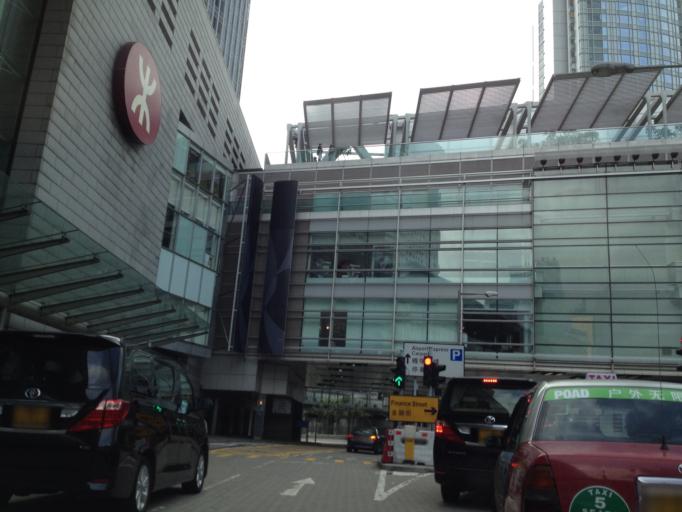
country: HK
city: Hong Kong
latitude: 22.2851
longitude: 114.1582
